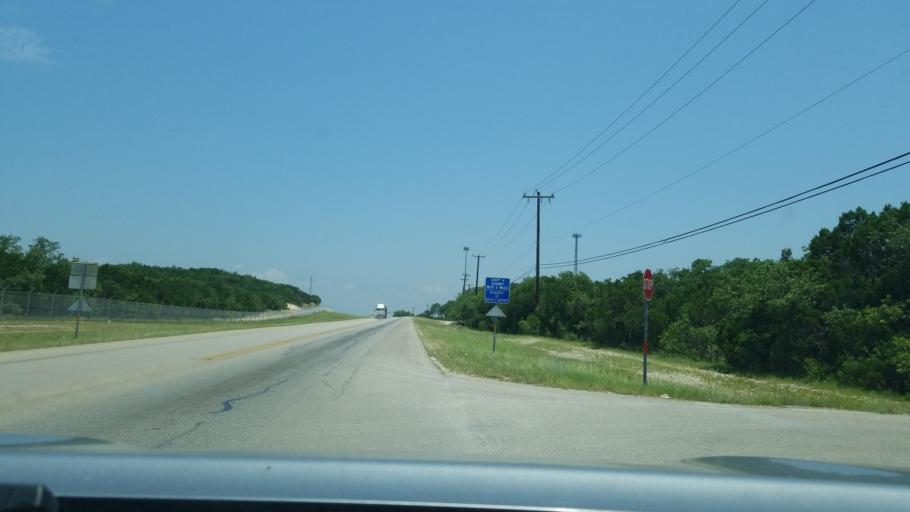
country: US
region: Texas
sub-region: Bexar County
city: Timberwood Park
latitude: 29.6973
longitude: -98.5212
